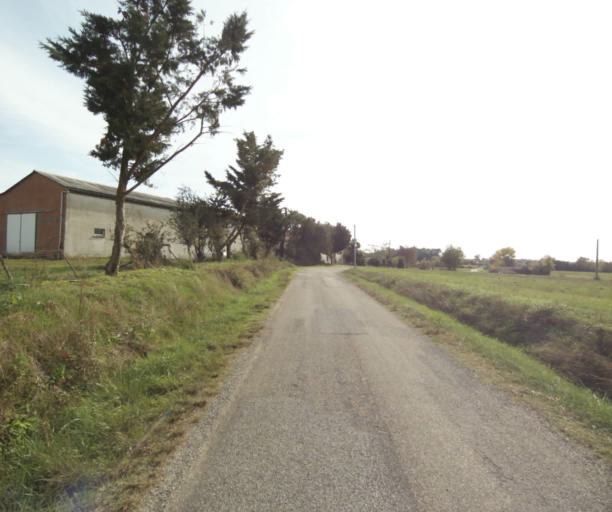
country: FR
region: Midi-Pyrenees
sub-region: Departement du Tarn-et-Garonne
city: Labastide-Saint-Pierre
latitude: 43.9029
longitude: 1.3852
